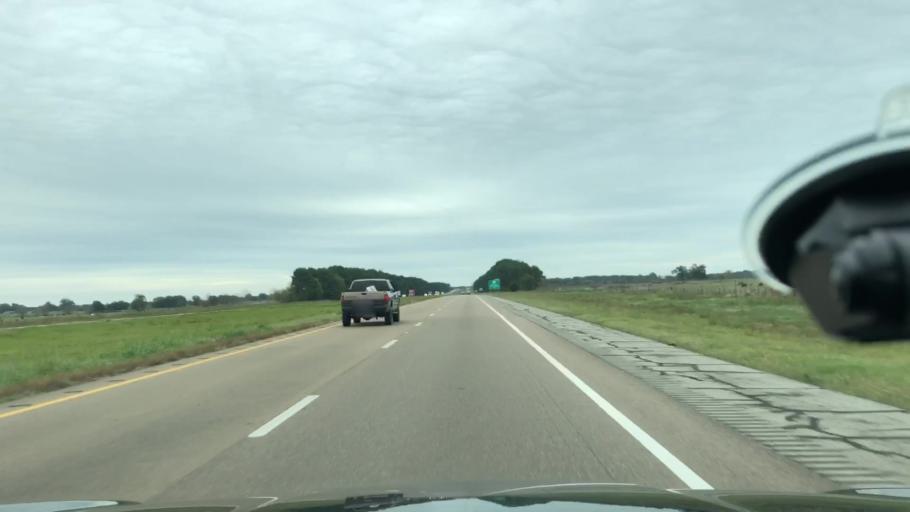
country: US
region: Texas
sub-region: Morris County
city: Omaha
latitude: 33.2909
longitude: -94.7693
